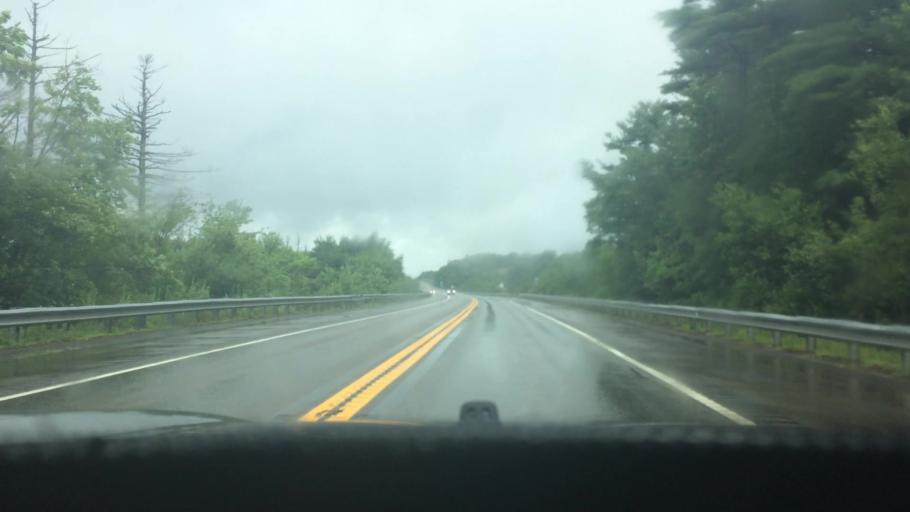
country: US
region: Massachusetts
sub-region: Worcester County
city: South Ashburnham
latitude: 42.5836
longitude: -71.9543
